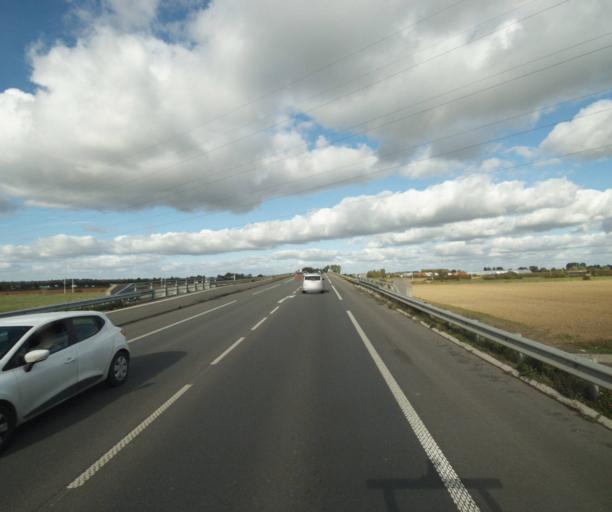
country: FR
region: Nord-Pas-de-Calais
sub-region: Departement du Nord
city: Houplines
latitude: 50.6735
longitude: 2.9156
